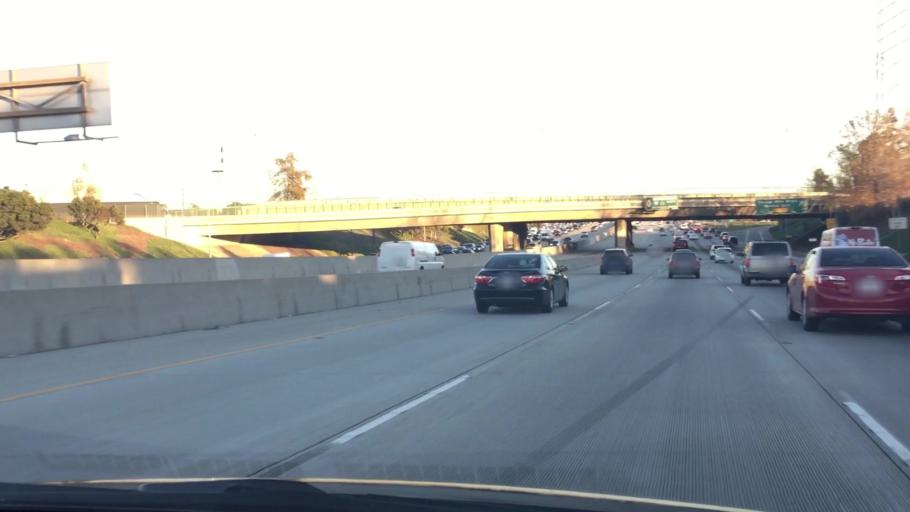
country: US
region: California
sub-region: Orange County
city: Santa Ana
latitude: 33.7572
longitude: -117.8576
